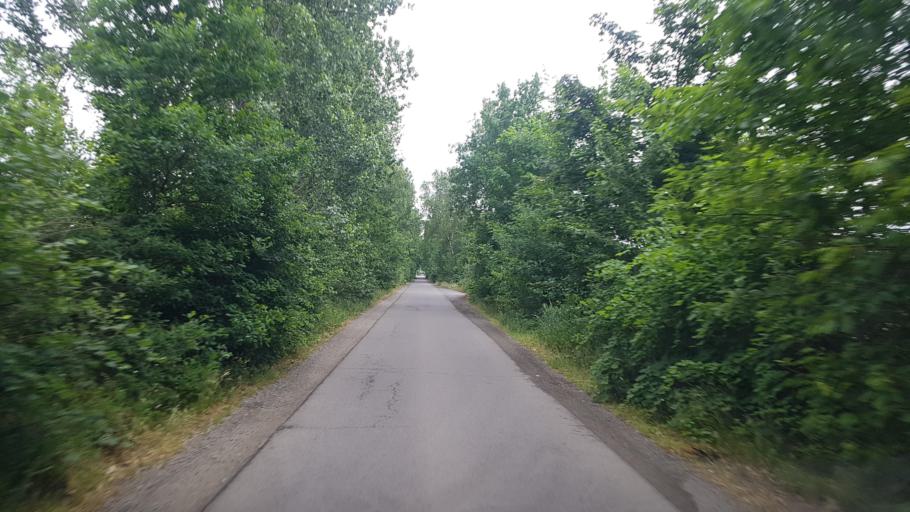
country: DE
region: Brandenburg
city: Schraden
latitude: 51.4307
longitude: 13.6940
